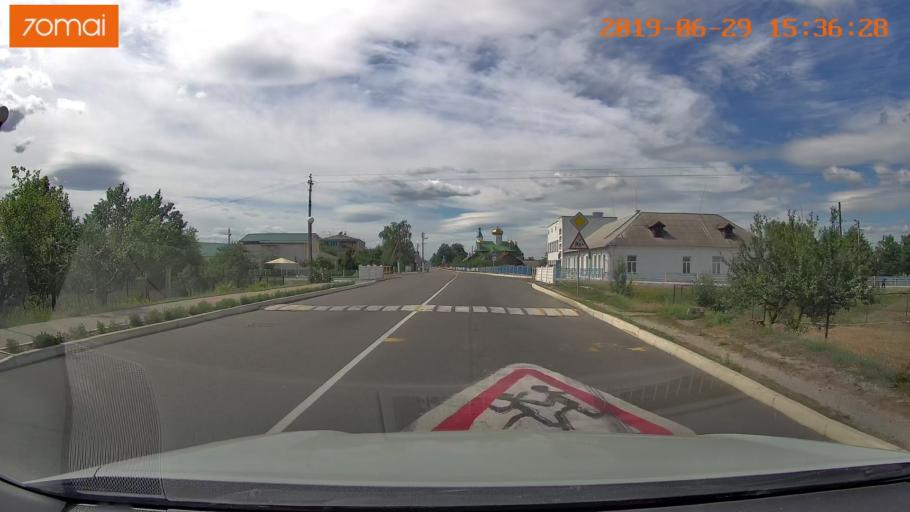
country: BY
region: Brest
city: Mikashevichy
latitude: 52.2208
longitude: 27.4679
